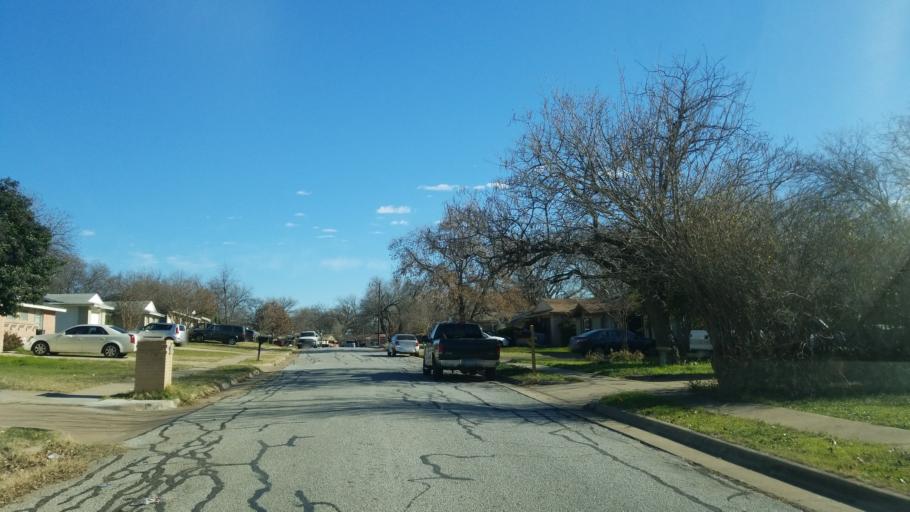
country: US
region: Texas
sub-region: Tarrant County
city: Arlington
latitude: 32.7309
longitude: -97.0601
